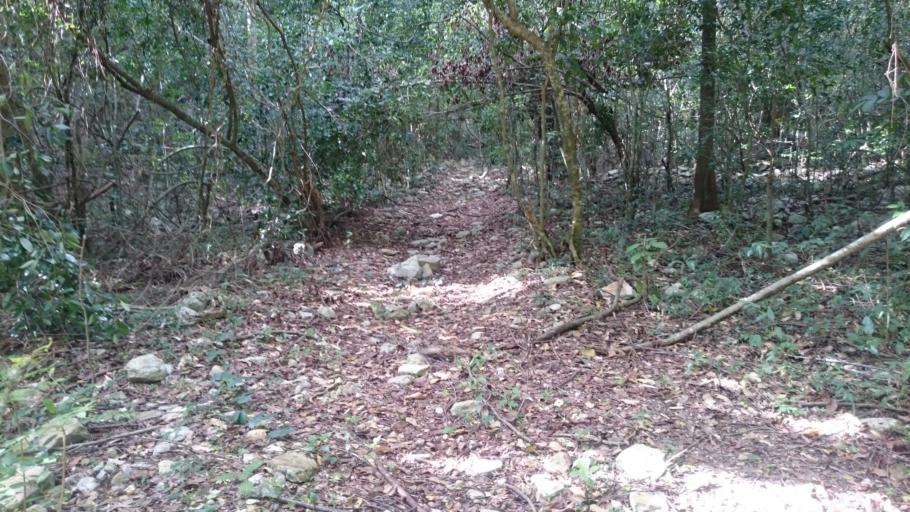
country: CU
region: Artemisa
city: Soroa
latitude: 22.8315
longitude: -82.9208
